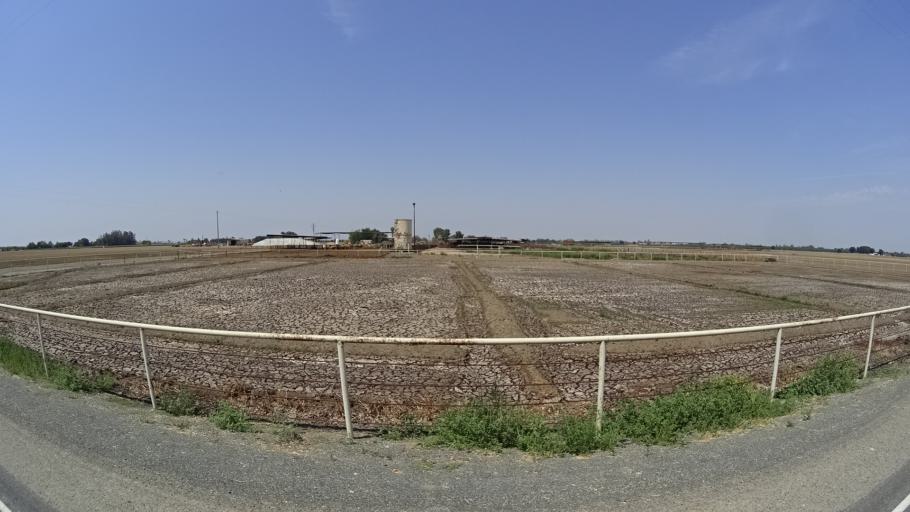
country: US
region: California
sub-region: Kings County
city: Lemoore
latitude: 36.3502
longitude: -119.7808
